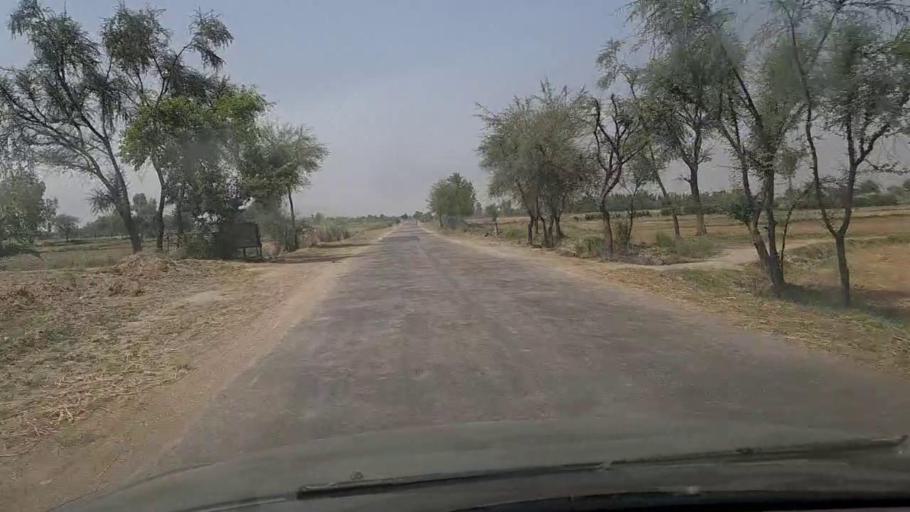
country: PK
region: Sindh
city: Khanpur
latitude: 27.8827
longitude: 69.4702
